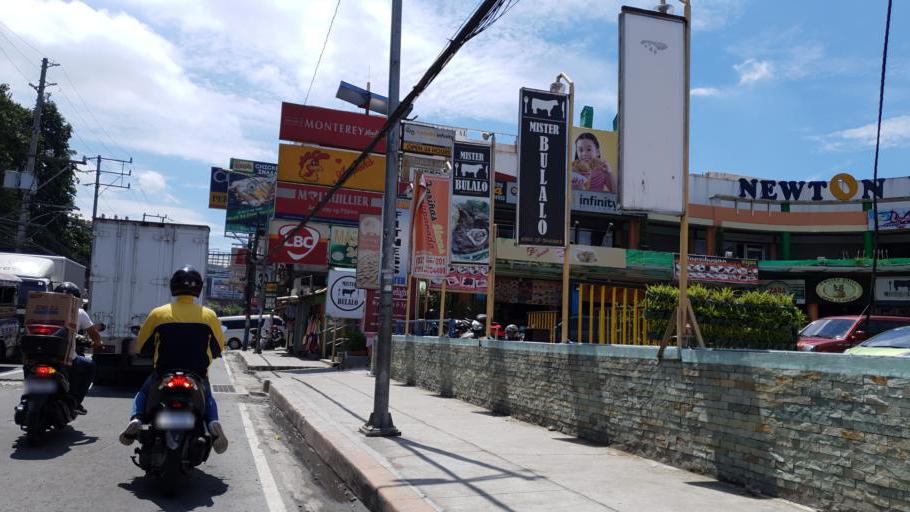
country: PH
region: Metro Manila
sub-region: San Juan
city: San Juan
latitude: 14.6015
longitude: 121.0125
